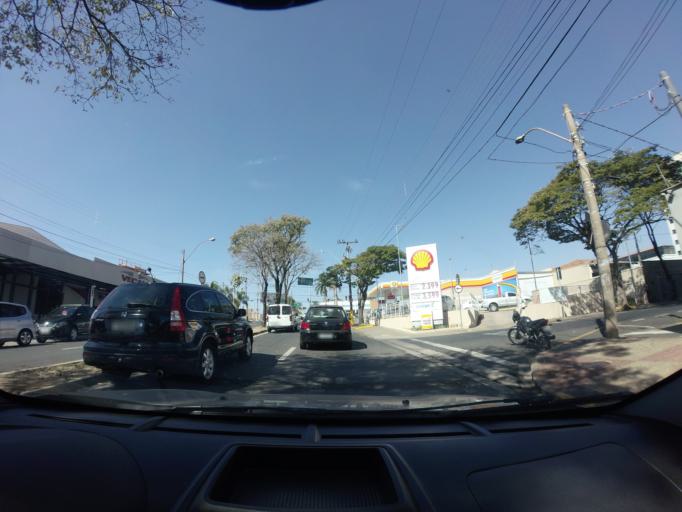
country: BR
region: Sao Paulo
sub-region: Piracicaba
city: Piracicaba
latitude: -22.7239
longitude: -47.6340
